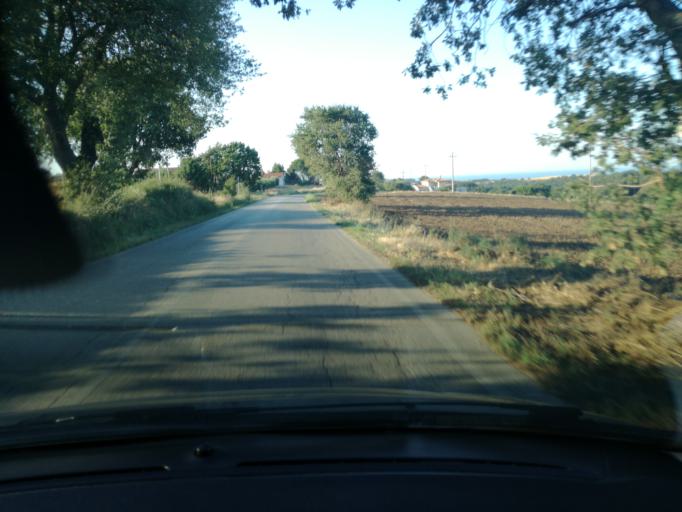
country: IT
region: Molise
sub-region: Provincia di Campobasso
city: San Giacomo degli Schiavoni
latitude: 41.9512
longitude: 14.9423
